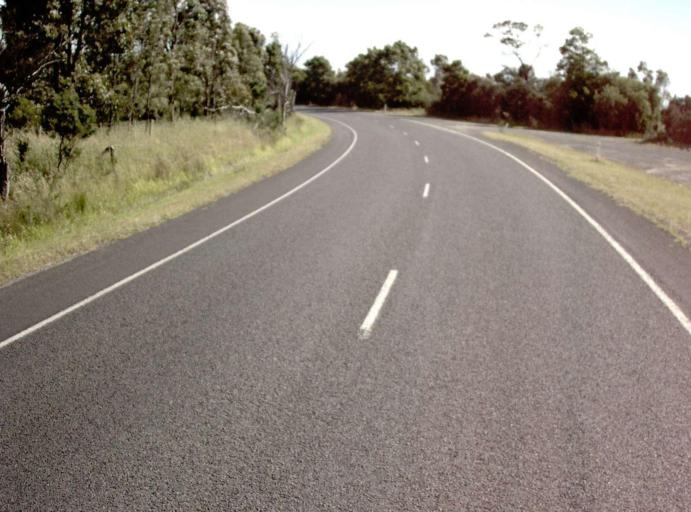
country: AU
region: Victoria
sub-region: Latrobe
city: Morwell
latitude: -38.1717
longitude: 146.4069
